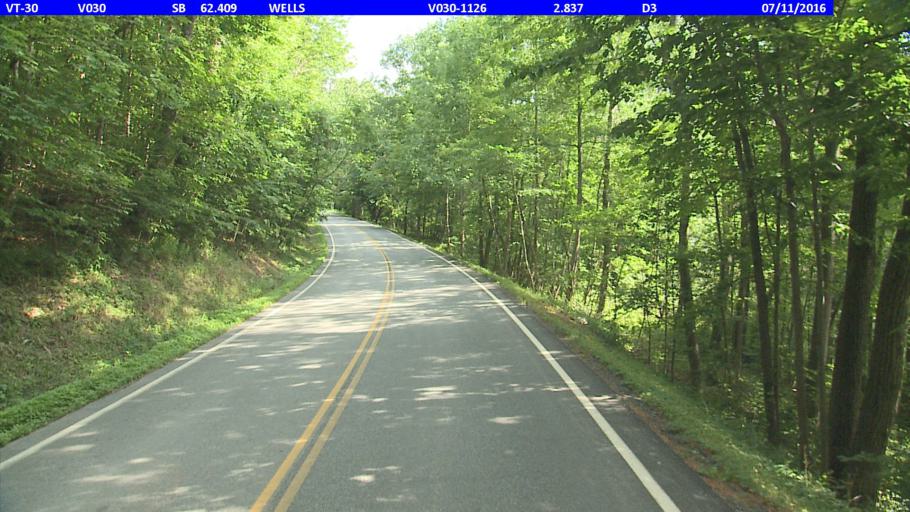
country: US
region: New York
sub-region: Washington County
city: Granville
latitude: 43.4349
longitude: -73.1959
